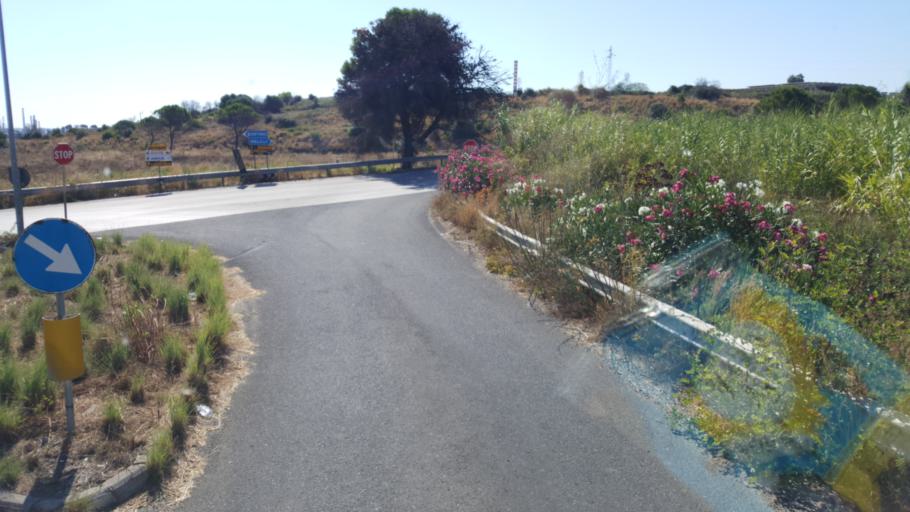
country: IT
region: Sicily
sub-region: Provincia di Siracusa
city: Melilli
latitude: 37.2168
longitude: 15.1531
